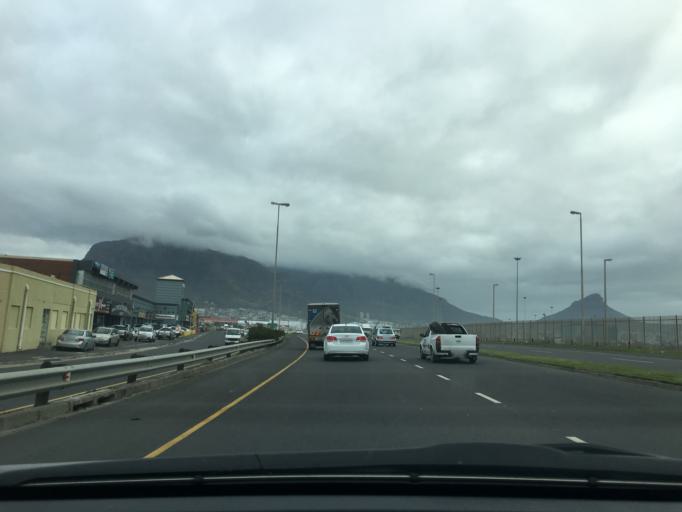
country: ZA
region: Western Cape
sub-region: City of Cape Town
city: Rosebank
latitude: -33.9107
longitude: 18.4698
